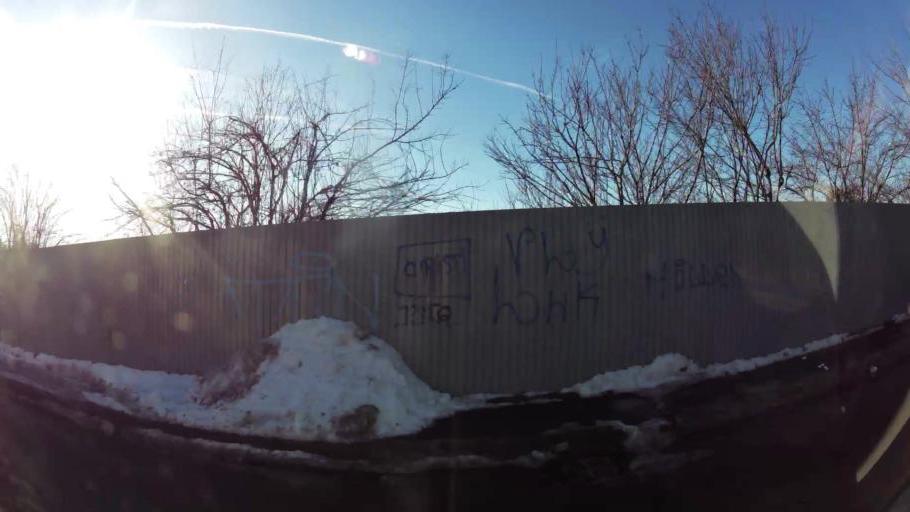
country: RO
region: Ilfov
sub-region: Comuna Fundeni-Dobroesti
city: Fundeni
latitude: 44.4784
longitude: 26.1435
